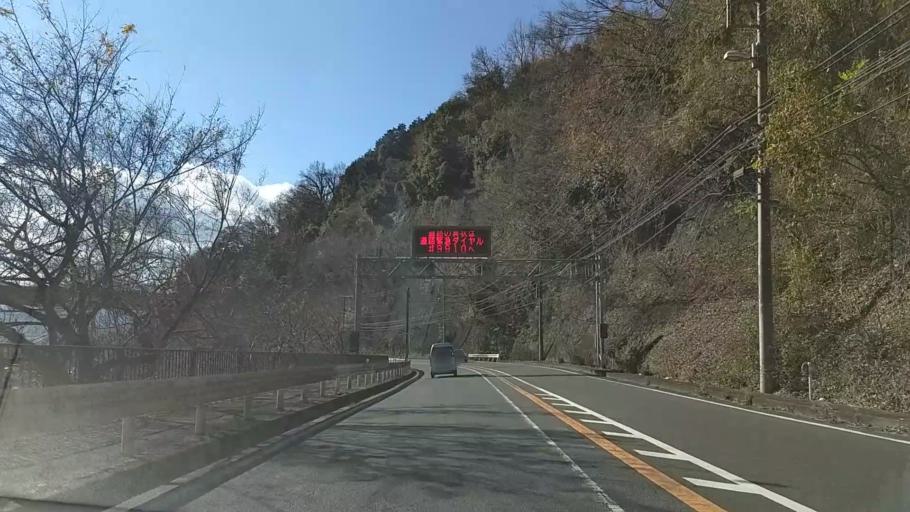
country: JP
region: Kanagawa
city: Hadano
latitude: 35.3518
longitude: 139.1507
